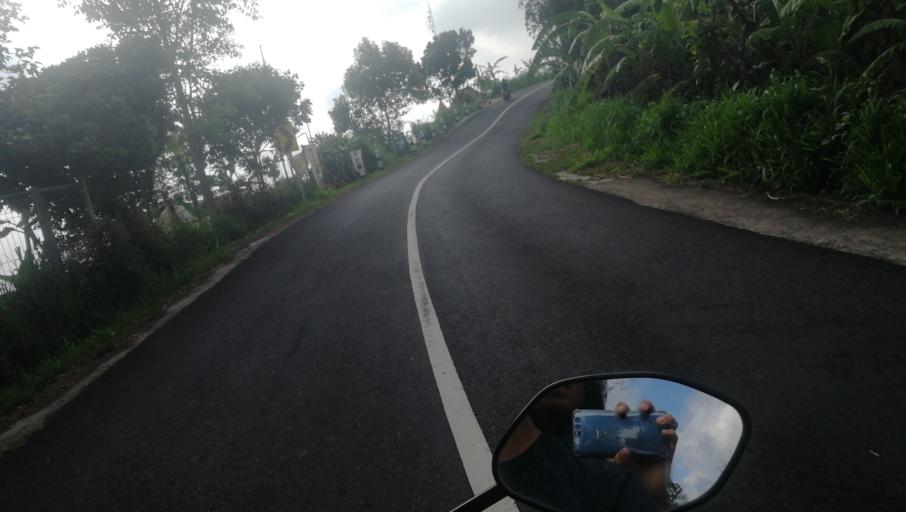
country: ID
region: Bali
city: Munduk
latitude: -8.2602
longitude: 115.0817
